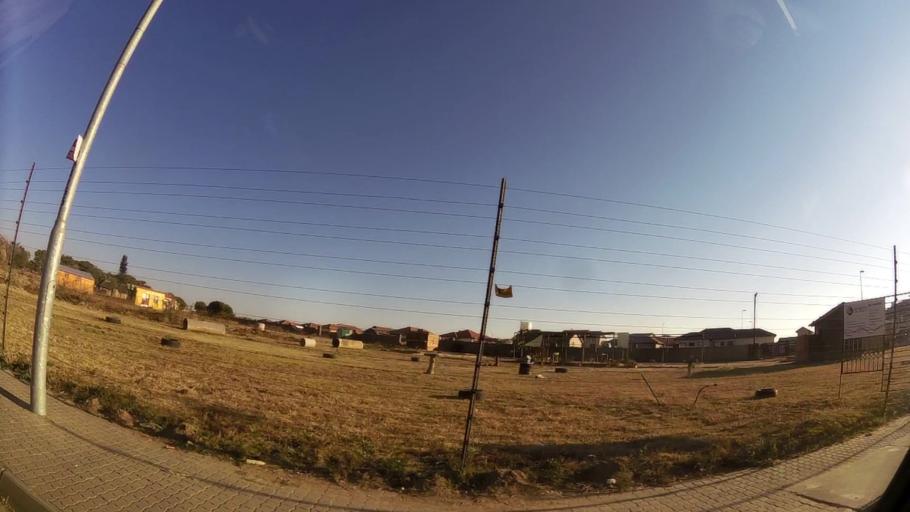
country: ZA
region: Gauteng
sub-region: City of Johannesburg Metropolitan Municipality
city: Midrand
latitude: -25.9298
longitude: 28.1016
